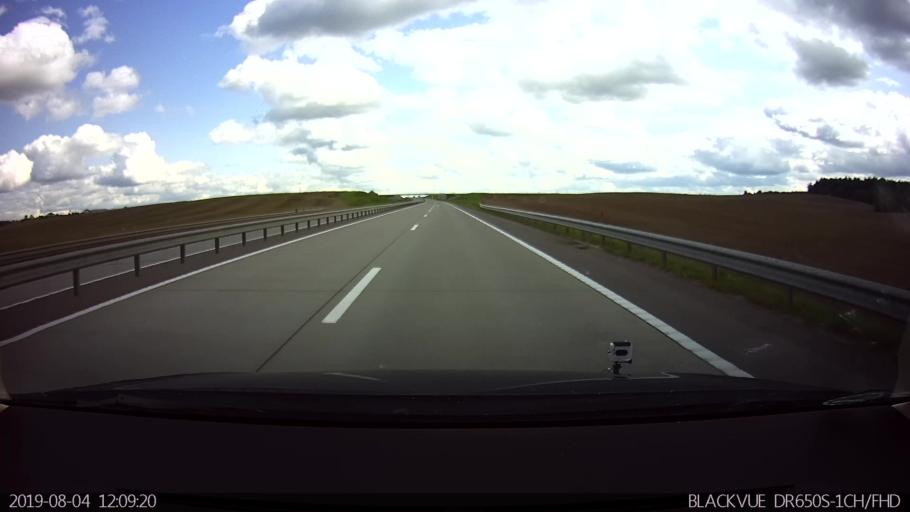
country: BY
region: Minsk
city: Syomkava
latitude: 54.0648
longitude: 27.4930
